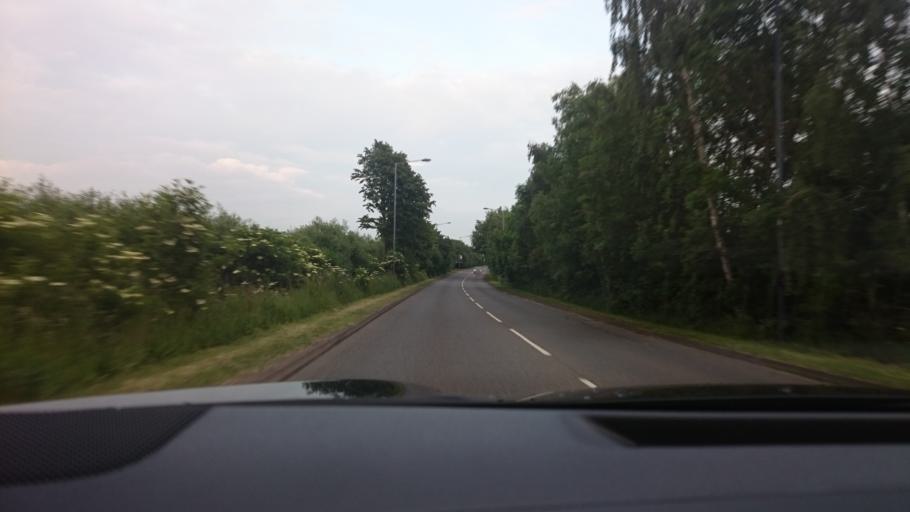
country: GB
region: England
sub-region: Warwickshire
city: Stratford-upon-Avon
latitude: 52.1832
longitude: -1.7063
